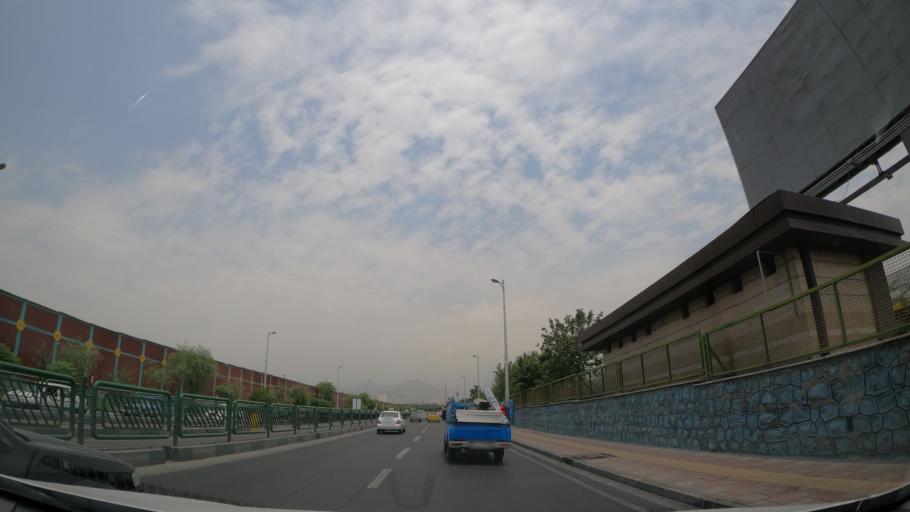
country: IR
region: Tehran
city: Tehran
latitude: 35.6906
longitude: 51.3405
